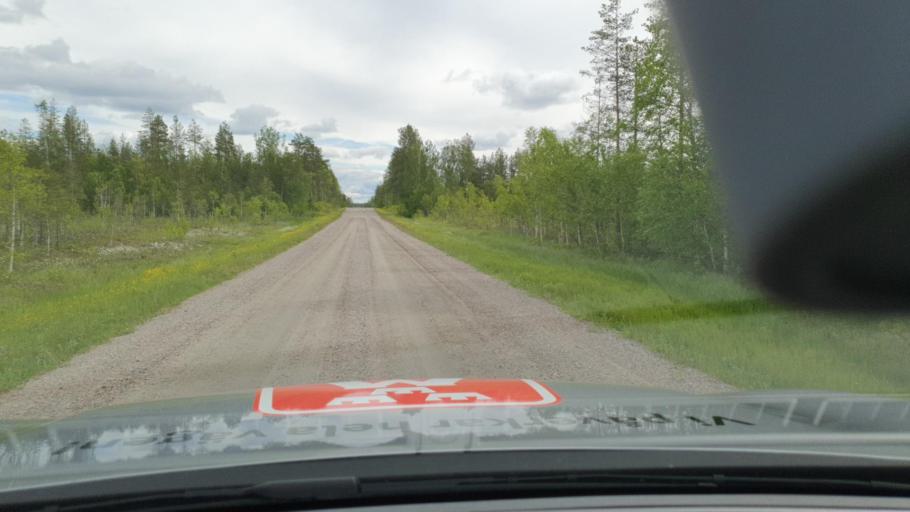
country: FI
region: Lapland
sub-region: Torniolaakso
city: Ylitornio
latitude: 65.9600
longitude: 23.6282
